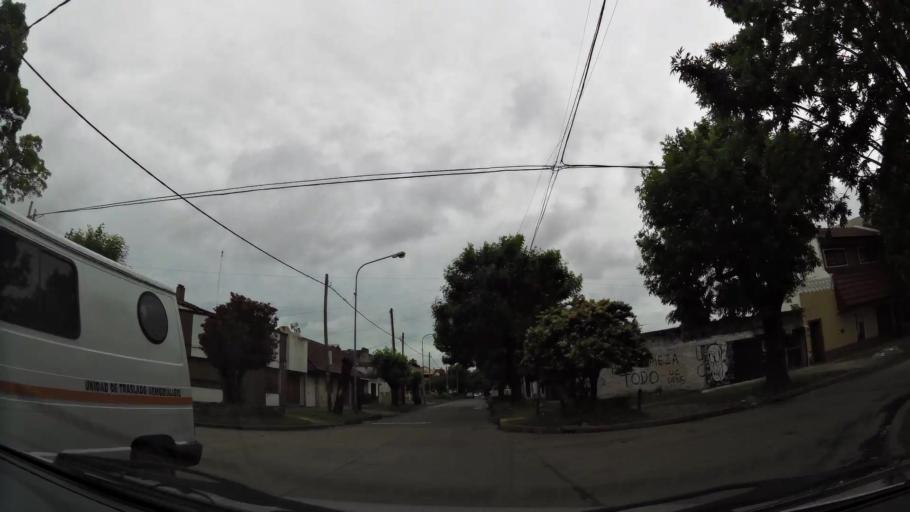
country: AR
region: Buenos Aires
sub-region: Partido de Lanus
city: Lanus
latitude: -34.7209
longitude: -58.3778
